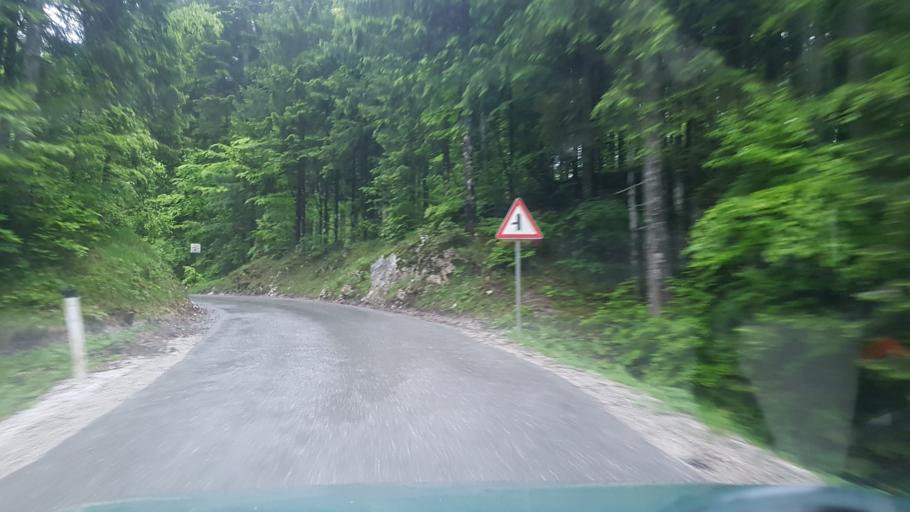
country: SI
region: Bohinj
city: Bohinjska Bistrica
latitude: 46.2748
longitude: 14.0214
